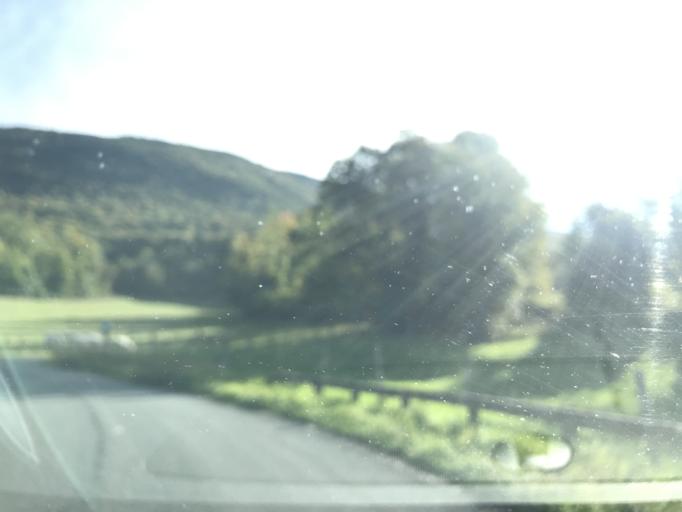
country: FR
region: Rhone-Alpes
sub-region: Departement de la Savoie
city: Novalaise
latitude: 45.6507
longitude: 5.7907
